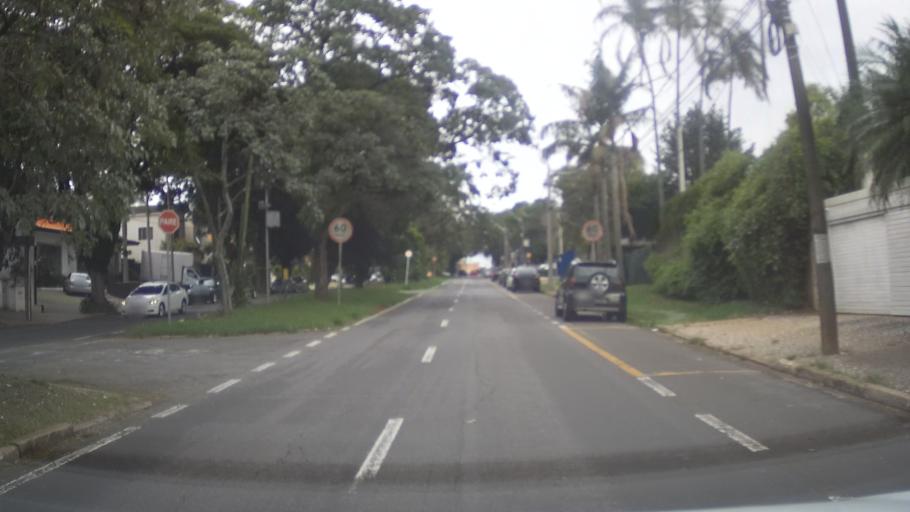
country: BR
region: Sao Paulo
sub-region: Campinas
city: Campinas
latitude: -22.9041
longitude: -47.0412
